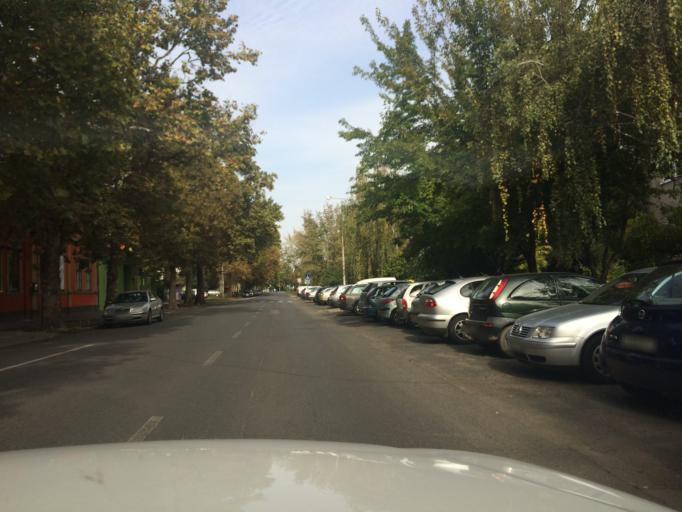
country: HU
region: Szabolcs-Szatmar-Bereg
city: Nyiregyhaza
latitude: 47.9624
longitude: 21.7117
